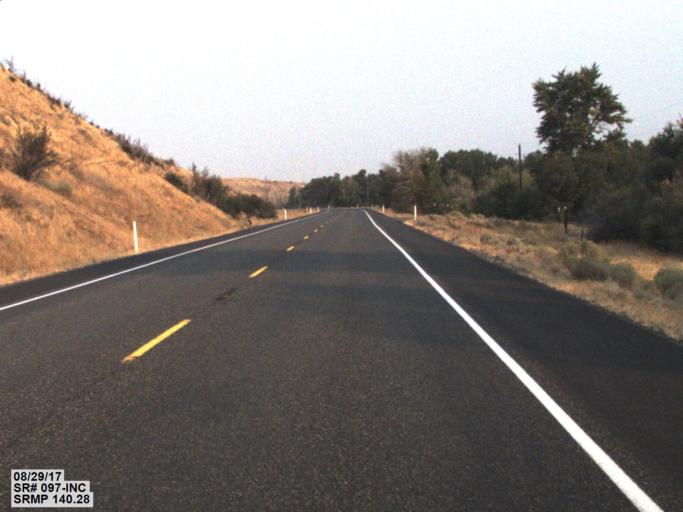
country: US
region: Washington
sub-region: Kittitas County
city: Ellensburg
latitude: 47.0822
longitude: -120.6406
